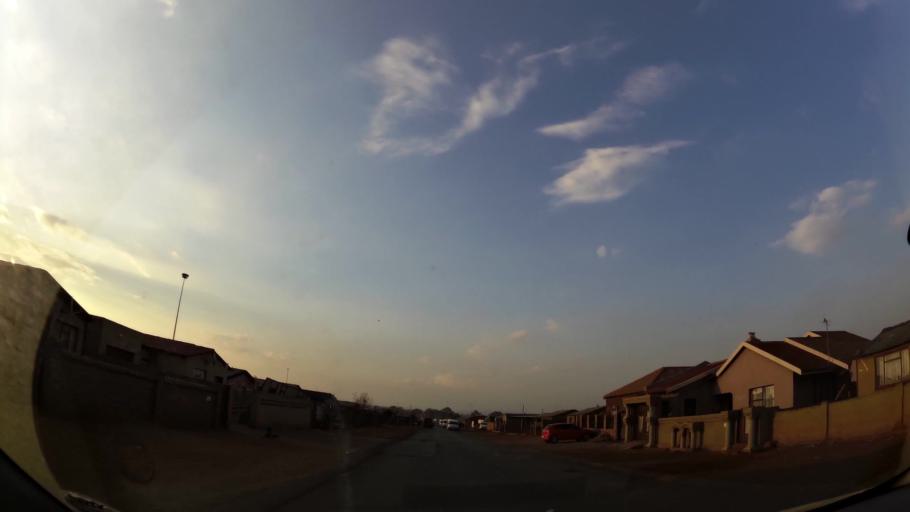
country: ZA
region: Gauteng
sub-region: City of Johannesburg Metropolitan Municipality
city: Orange Farm
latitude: -26.5545
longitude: 27.8630
